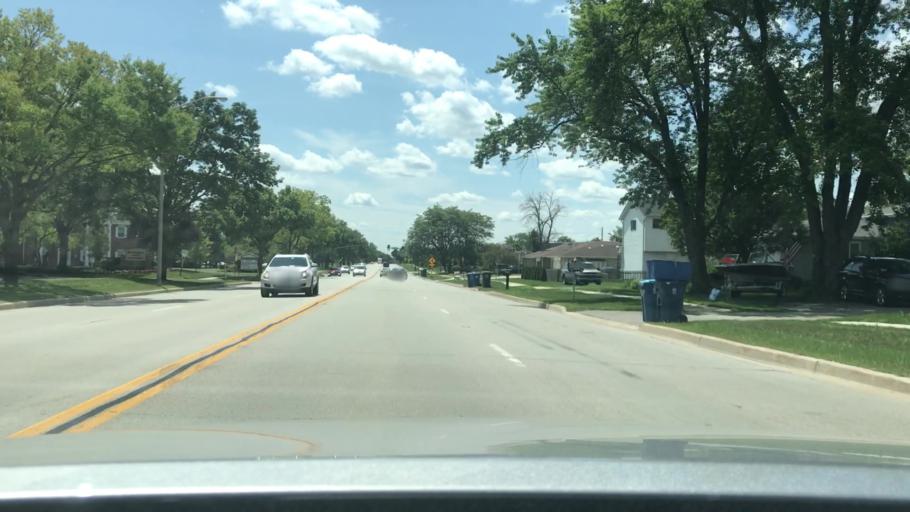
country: US
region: Illinois
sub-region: DuPage County
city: Darien
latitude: 41.7677
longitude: -88.0084
